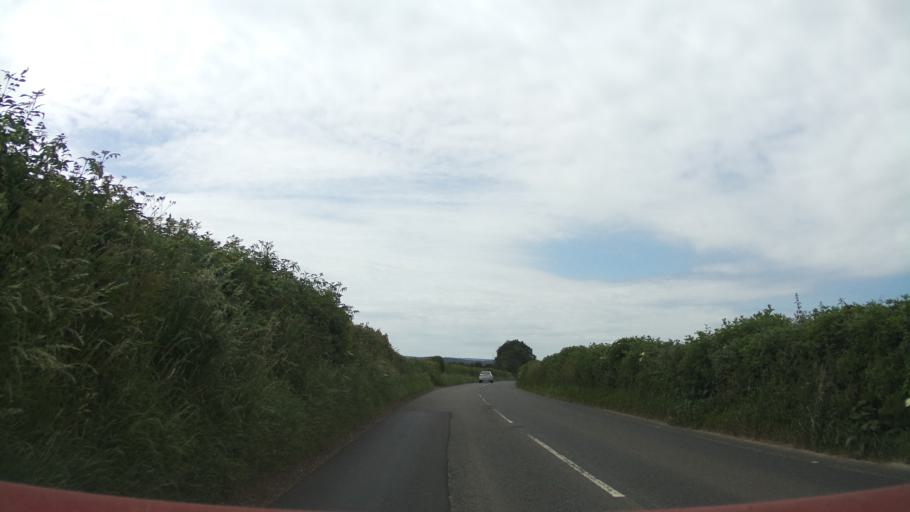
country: GB
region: England
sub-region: Dorset
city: Sherborne
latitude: 50.9684
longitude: -2.5138
